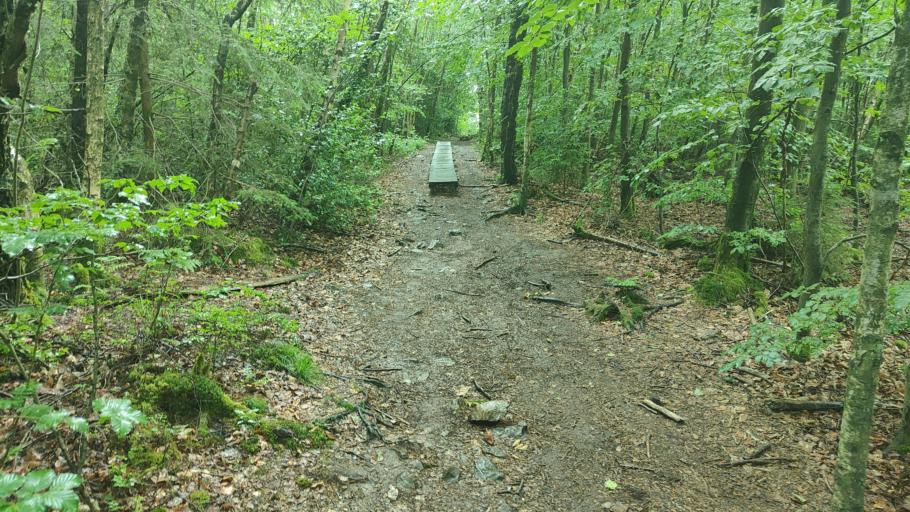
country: DE
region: North Rhine-Westphalia
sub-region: Regierungsbezirk Koln
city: Roetgen
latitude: 50.6294
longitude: 6.1808
